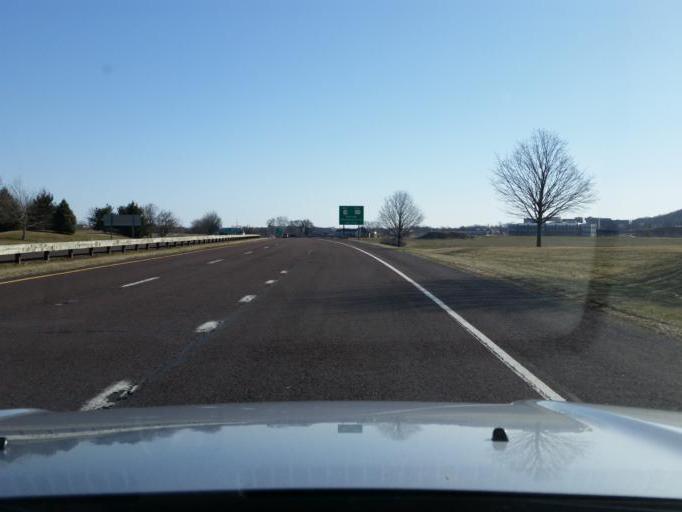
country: US
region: Pennsylvania
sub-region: Dauphin County
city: Hummelstown
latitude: 40.2600
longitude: -76.6961
